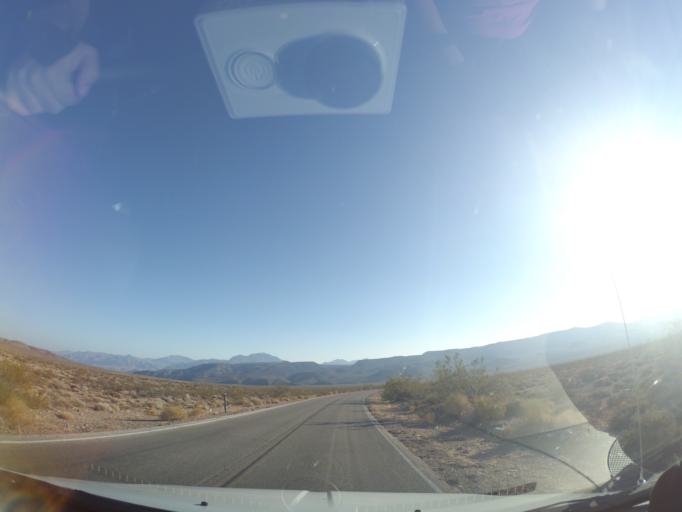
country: US
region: Nevada
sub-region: Nye County
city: Beatty
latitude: 36.2465
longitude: -116.6820
